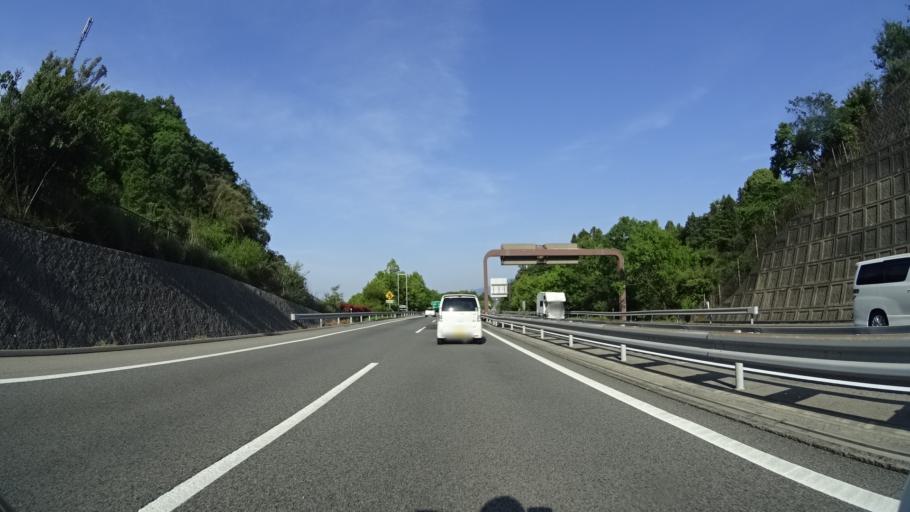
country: JP
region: Ehime
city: Saijo
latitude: 33.8853
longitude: 133.0993
